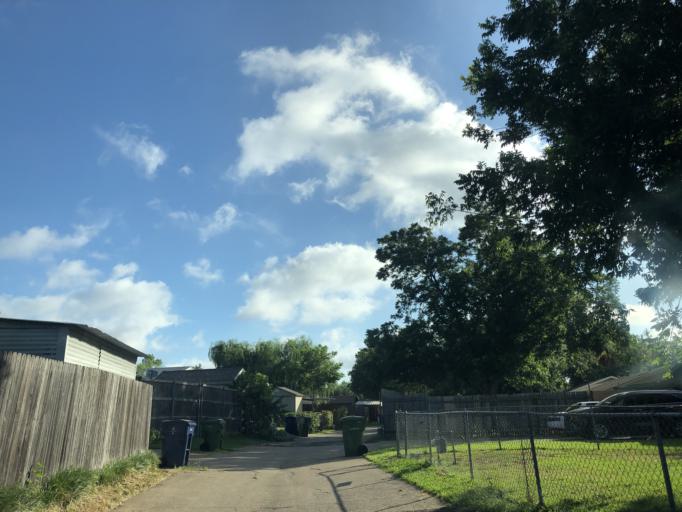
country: US
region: Texas
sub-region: Dallas County
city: Garland
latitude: 32.8514
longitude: -96.6400
